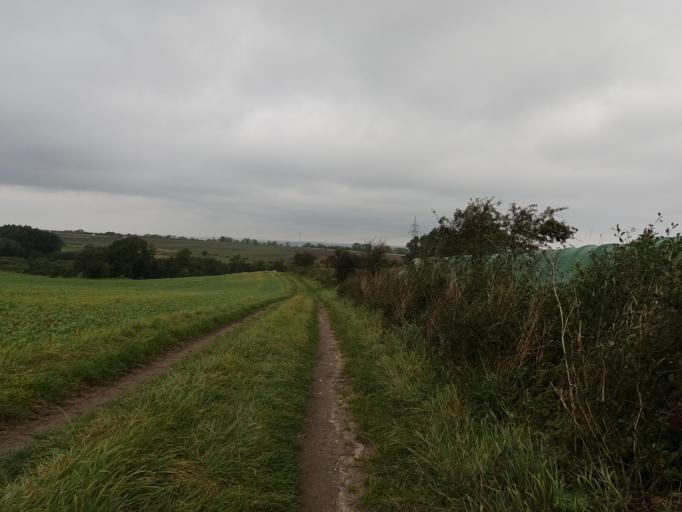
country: DE
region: Schleswig-Holstein
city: Heiligenhafen
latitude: 54.3555
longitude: 11.0017
